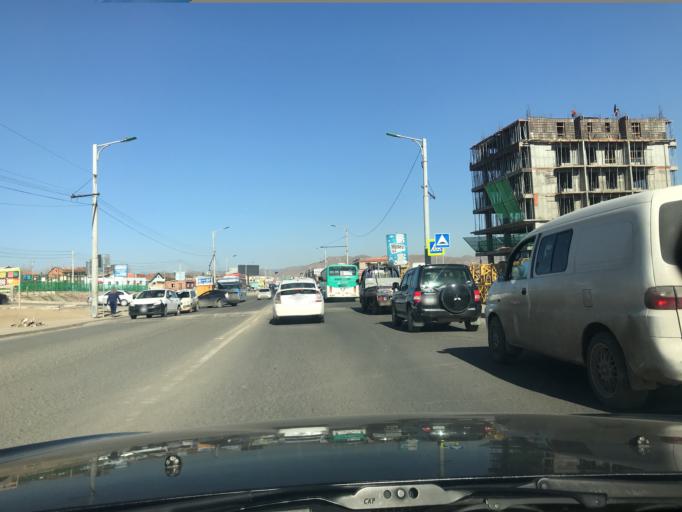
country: MN
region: Ulaanbaatar
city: Ulaanbaatar
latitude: 47.9348
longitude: 106.9073
